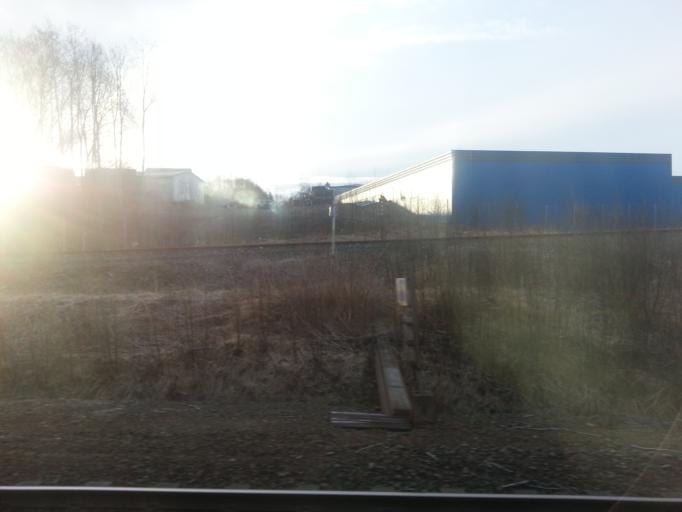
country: NO
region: Sor-Trondelag
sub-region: Trondheim
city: Trondheim
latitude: 63.3472
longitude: 10.3549
